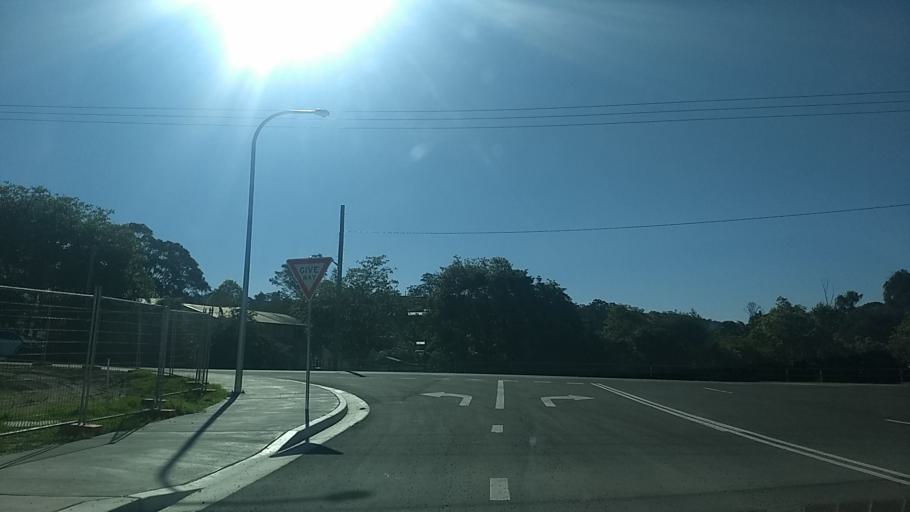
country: AU
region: New South Wales
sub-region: Bega Valley
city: Merimbula
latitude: -36.8851
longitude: 149.9075
